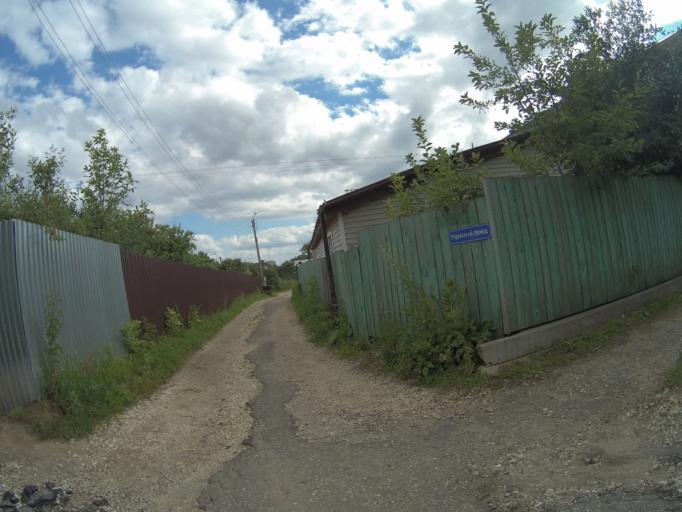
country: RU
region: Vladimir
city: Vladimir
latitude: 56.1167
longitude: 40.3703
